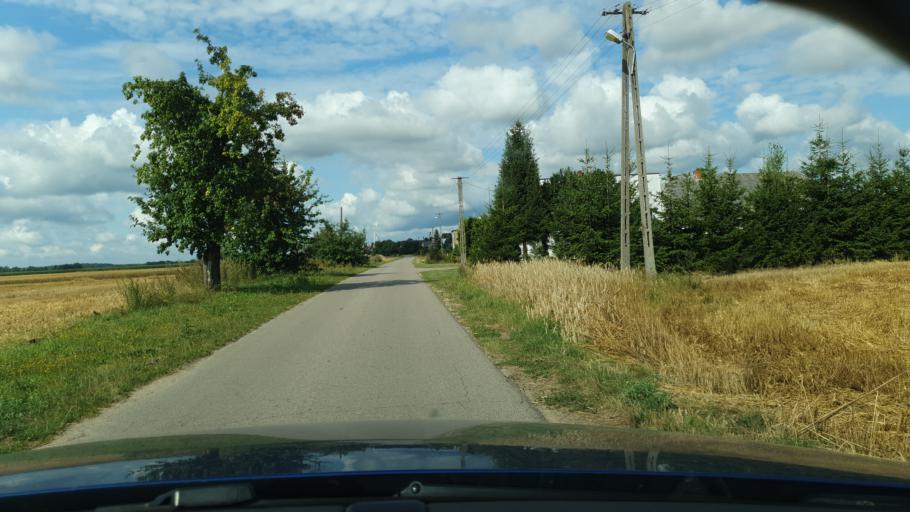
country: PL
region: Pomeranian Voivodeship
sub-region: Powiat czluchowski
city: Przechlewo
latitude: 53.8097
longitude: 17.3880
